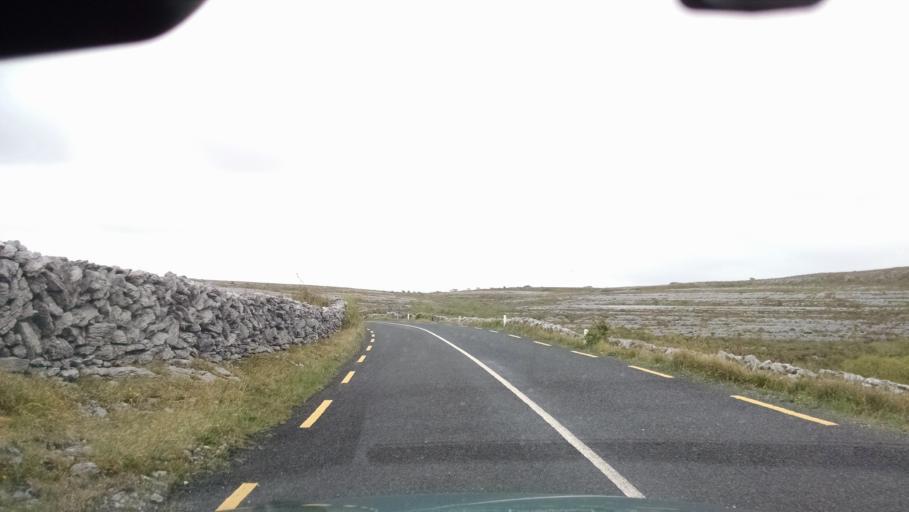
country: IE
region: Connaught
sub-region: County Galway
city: Bearna
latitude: 53.0784
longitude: -9.1640
